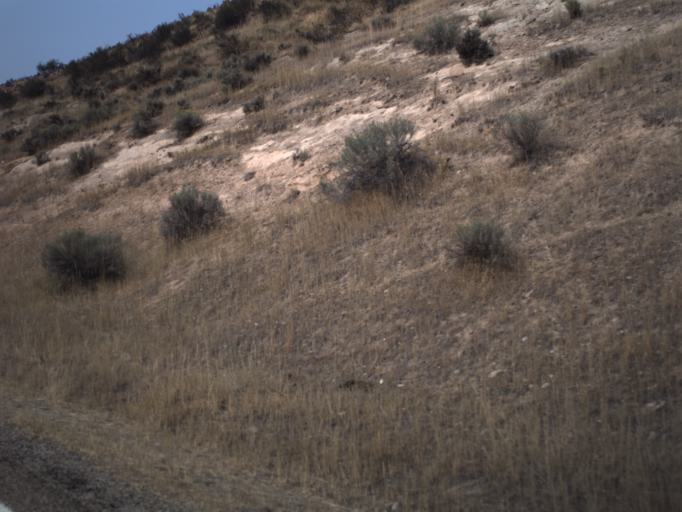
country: US
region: Utah
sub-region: Morgan County
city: Morgan
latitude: 40.9346
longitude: -111.5677
